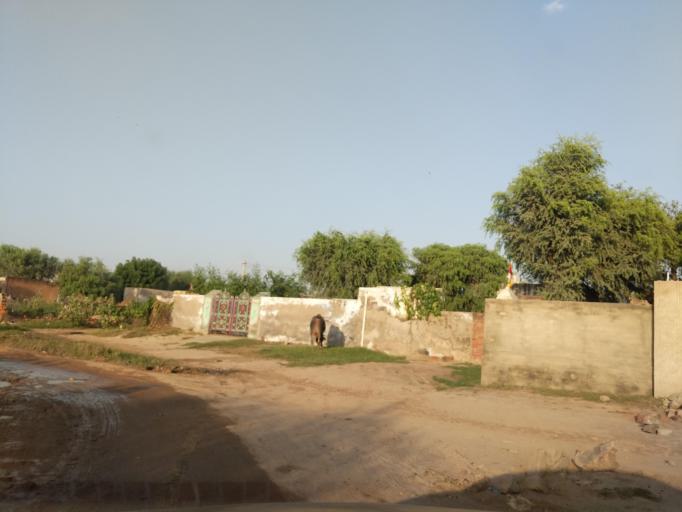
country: IN
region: Rajasthan
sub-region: Churu
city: Rajgarh
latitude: 28.5631
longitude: 75.3662
